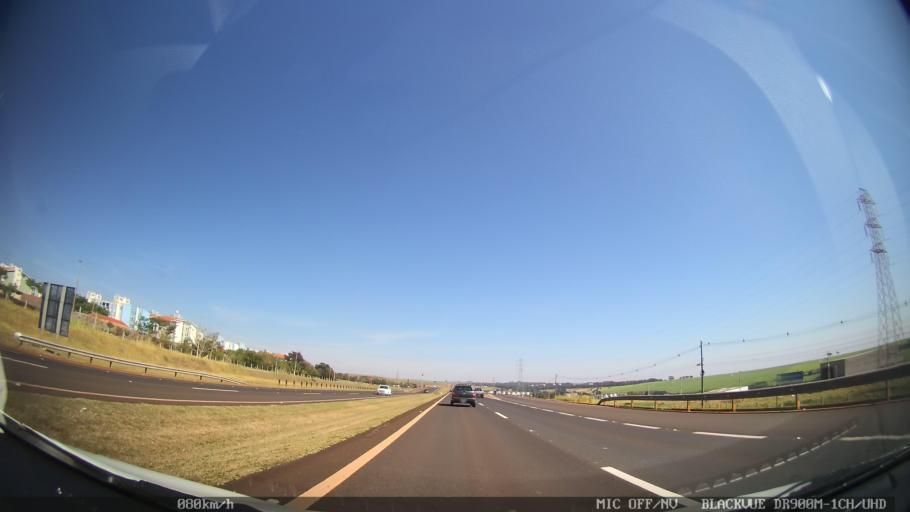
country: BR
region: Sao Paulo
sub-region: Ribeirao Preto
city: Ribeirao Preto
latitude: -21.1319
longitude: -47.8533
